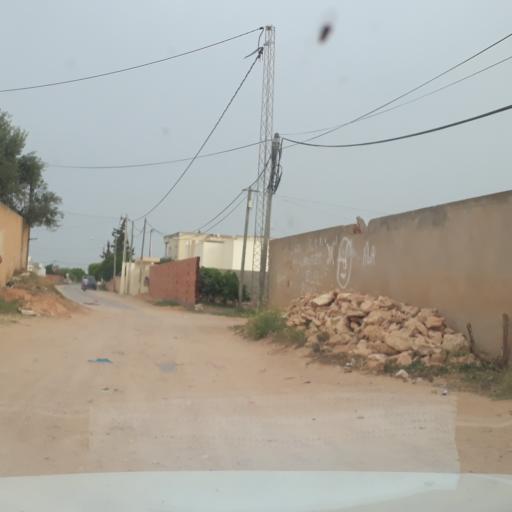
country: TN
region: Safaqis
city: Al Qarmadah
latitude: 34.8181
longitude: 10.7713
